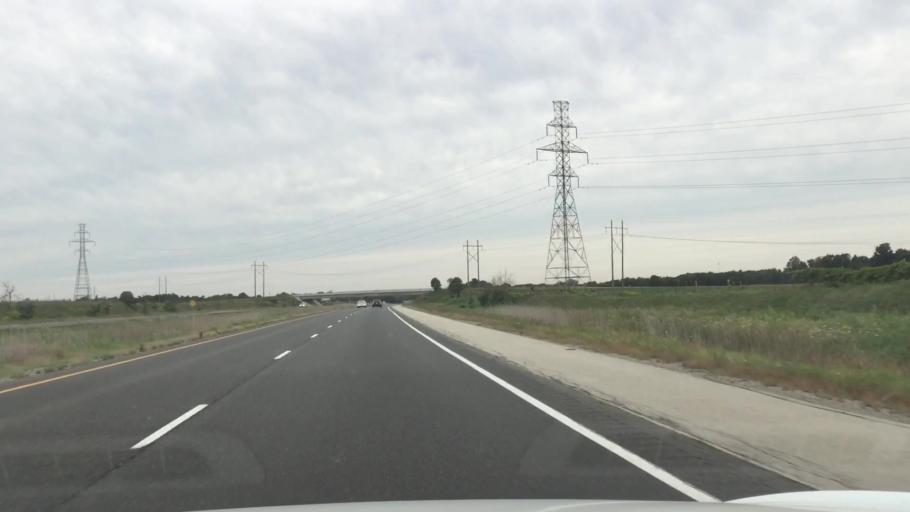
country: CA
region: Ontario
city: Delaware
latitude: 42.8896
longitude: -81.3547
